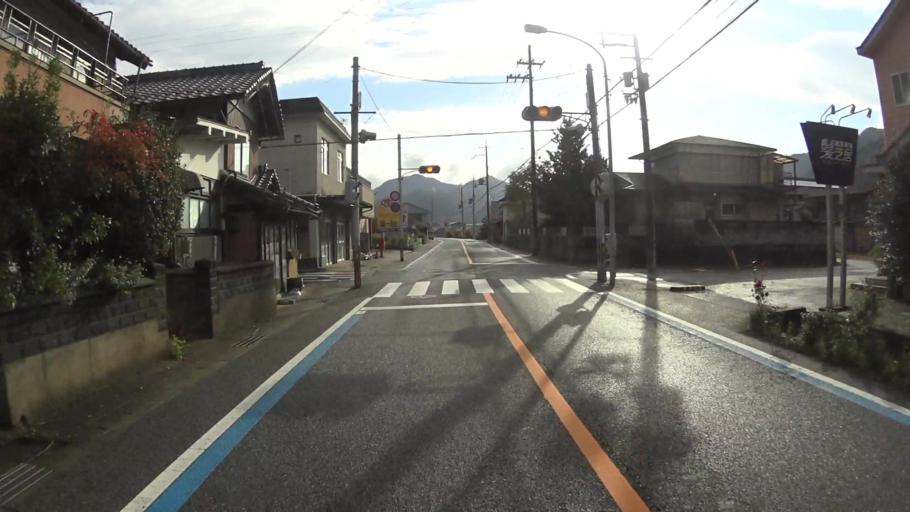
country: JP
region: Kyoto
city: Ayabe
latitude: 35.3039
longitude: 135.1937
